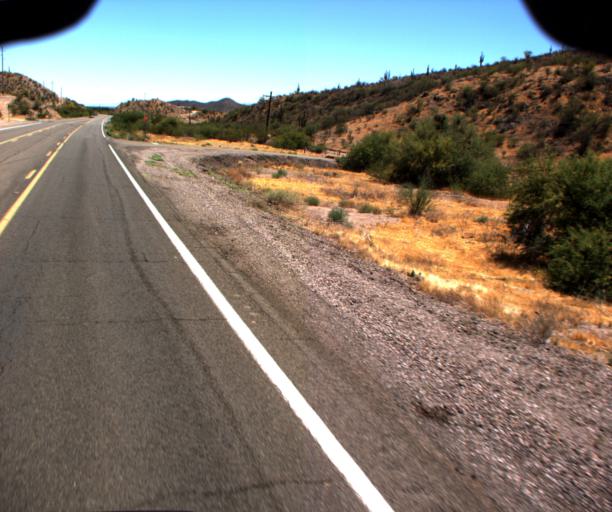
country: US
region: Arizona
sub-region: Pinal County
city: Kearny
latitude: 32.9487
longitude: -110.7430
